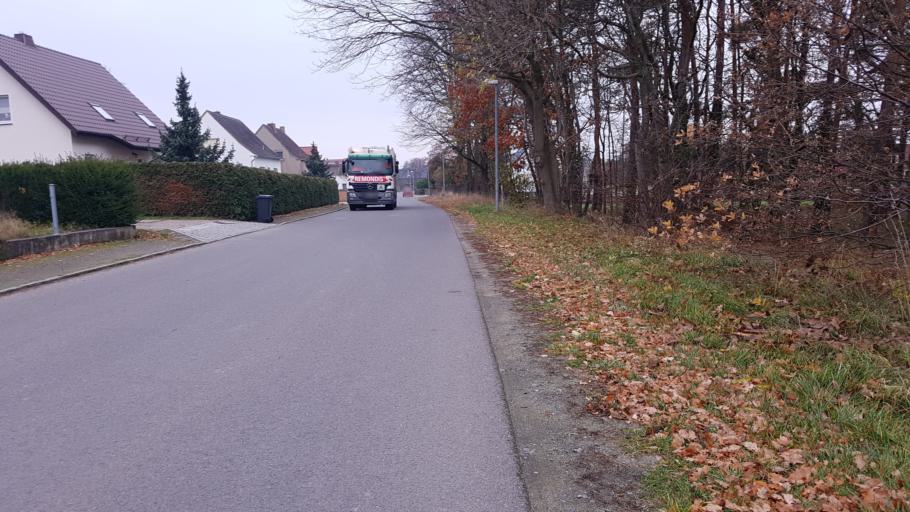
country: DE
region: Brandenburg
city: Grosskmehlen
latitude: 51.3745
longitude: 13.7307
